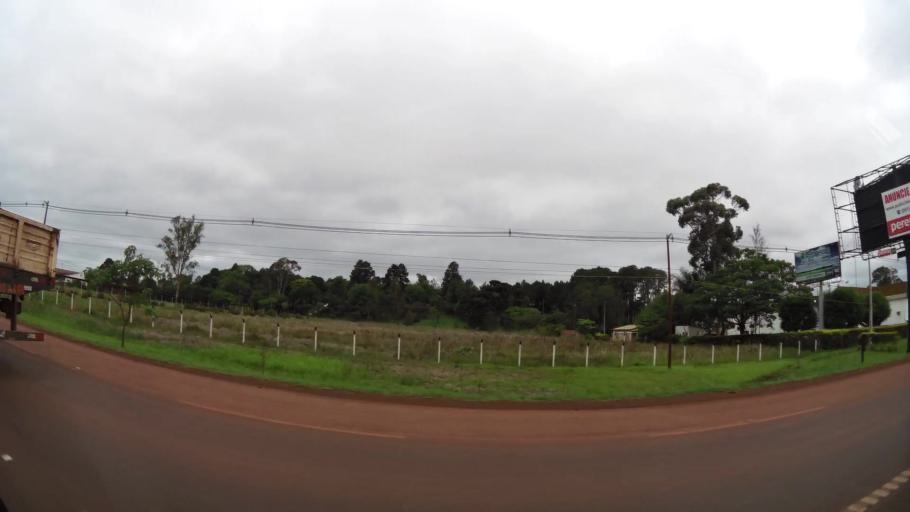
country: PY
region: Alto Parana
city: Presidente Franco
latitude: -25.4907
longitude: -54.7724
